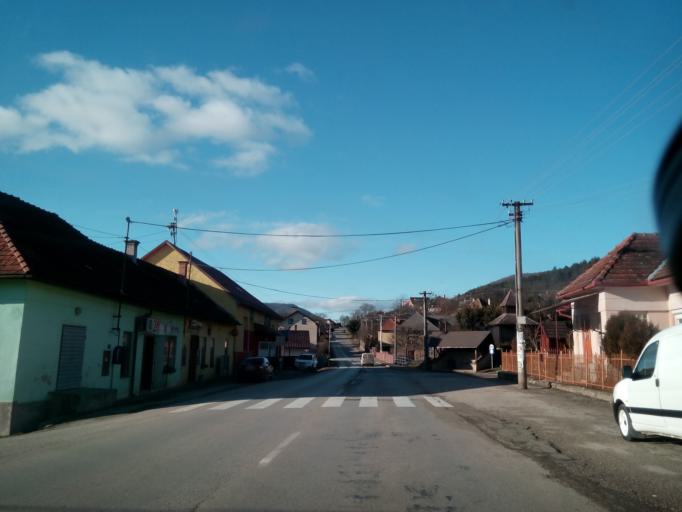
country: SK
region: Kosicky
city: Roznava
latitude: 48.6594
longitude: 20.4902
